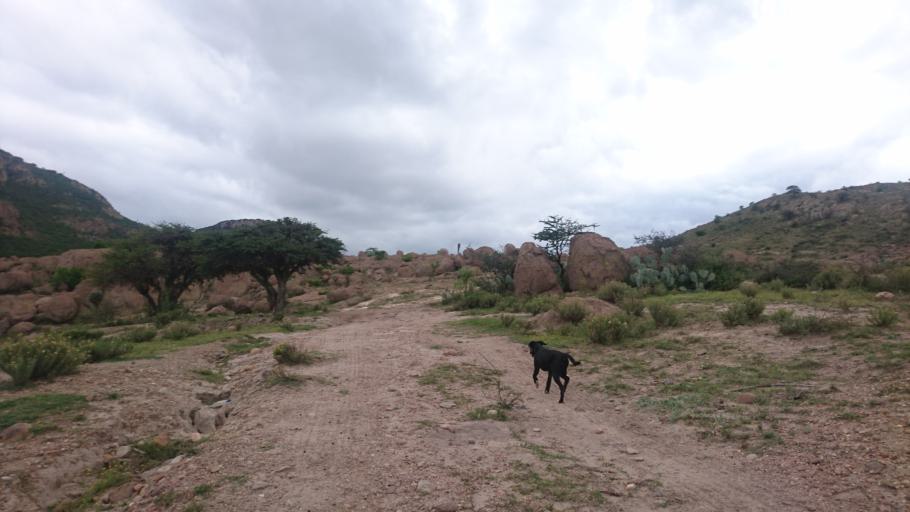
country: MX
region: San Luis Potosi
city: Escalerillas
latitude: 22.0745
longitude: -101.0970
